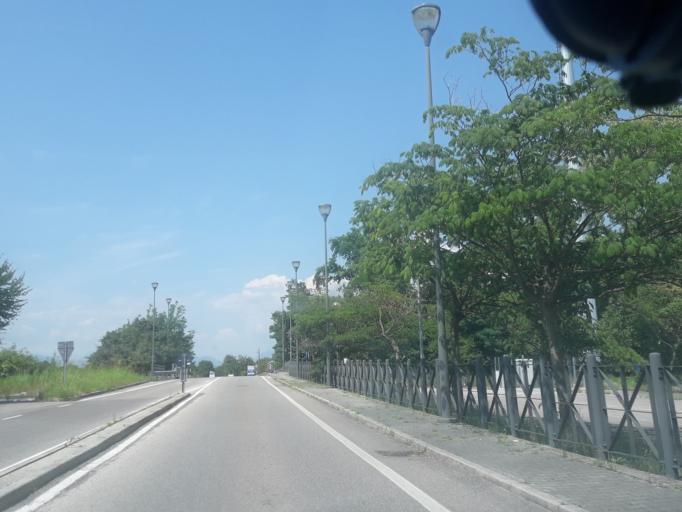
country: IT
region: Friuli Venezia Giulia
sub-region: Provincia di Udine
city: Colugna
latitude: 46.0885
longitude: 13.1831
